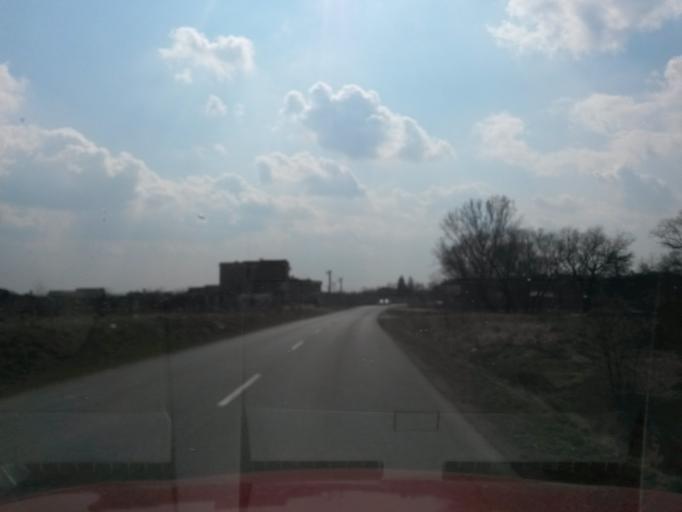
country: SK
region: Kosicky
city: Kosice
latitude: 48.6026
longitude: 21.1714
